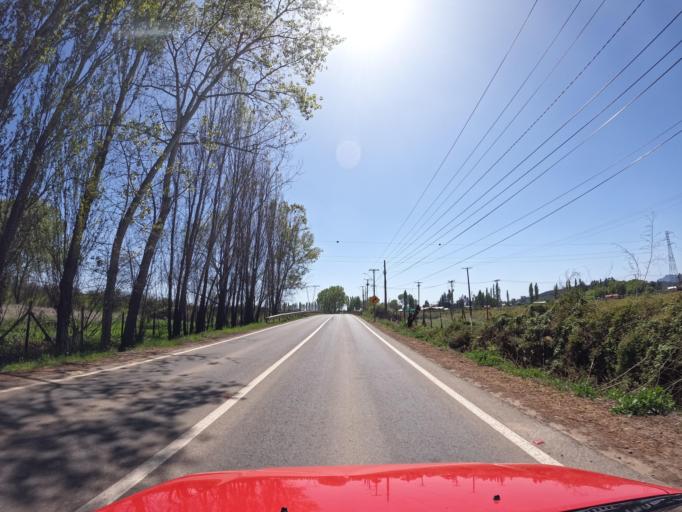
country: CL
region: Maule
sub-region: Provincia de Linares
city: Colbun
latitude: -35.7465
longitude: -71.4210
